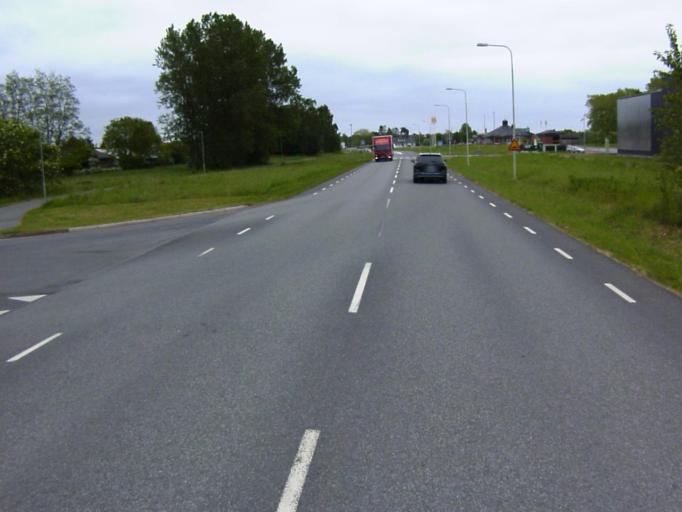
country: SE
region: Skane
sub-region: Kristianstads Kommun
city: Ahus
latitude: 55.9344
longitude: 14.2840
